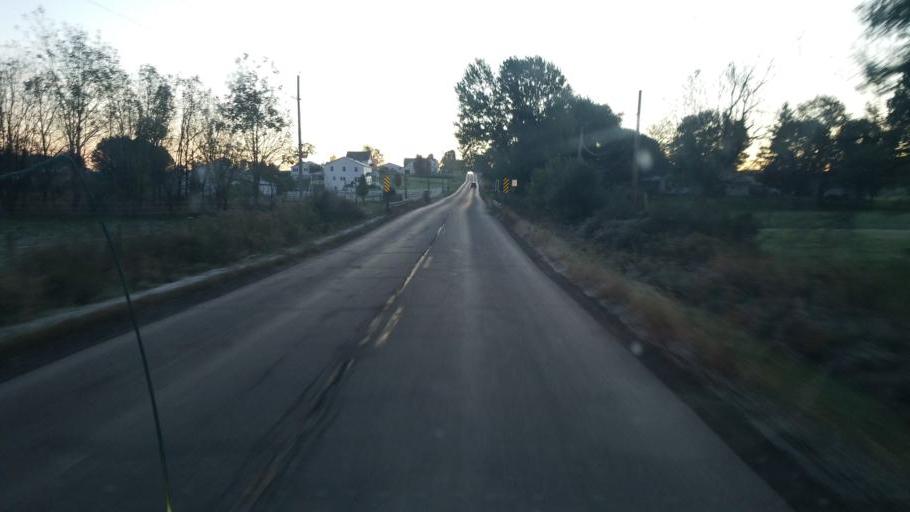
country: US
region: Ohio
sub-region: Wayne County
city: Apple Creek
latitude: 40.7411
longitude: -81.7842
